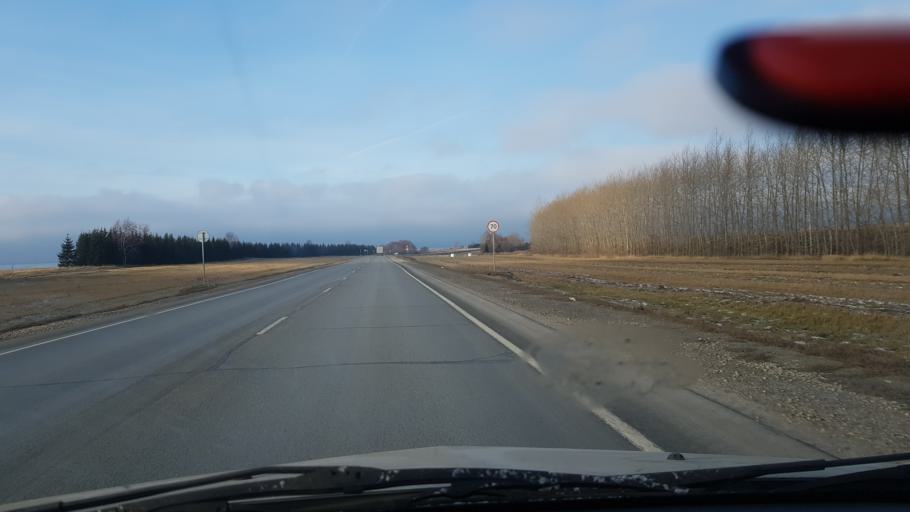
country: RU
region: Tatarstan
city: Laishevo
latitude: 55.3966
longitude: 49.7743
